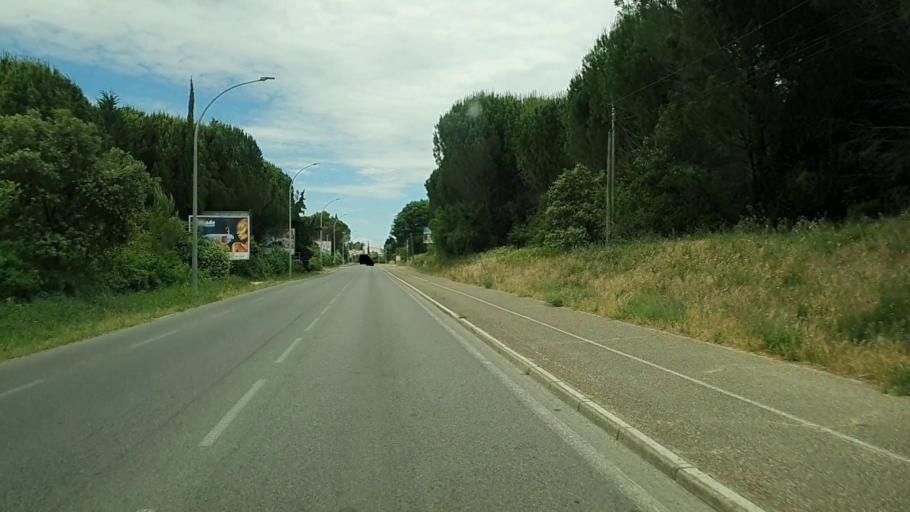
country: FR
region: Languedoc-Roussillon
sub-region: Departement du Gard
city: Bagnols-sur-Ceze
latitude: 44.1494
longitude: 4.6124
